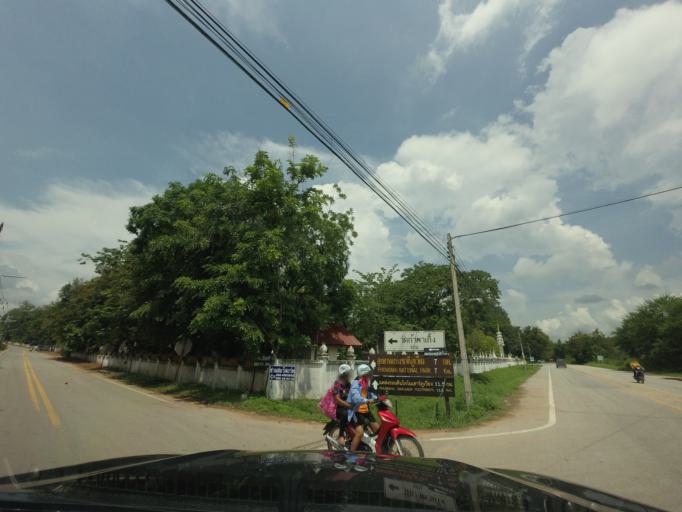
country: TH
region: Khon Kaen
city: Wiang Kao
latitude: 16.6770
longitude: 102.2970
